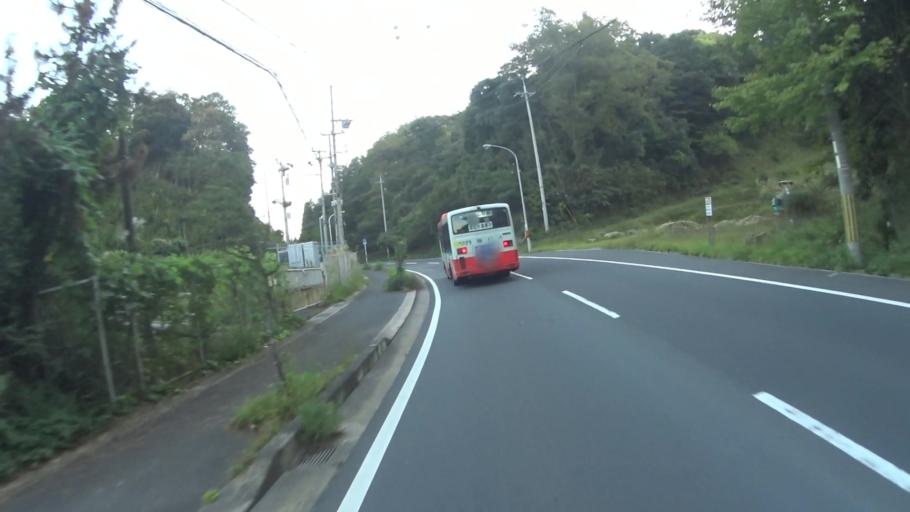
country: JP
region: Kyoto
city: Miyazu
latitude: 35.6350
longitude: 135.0538
